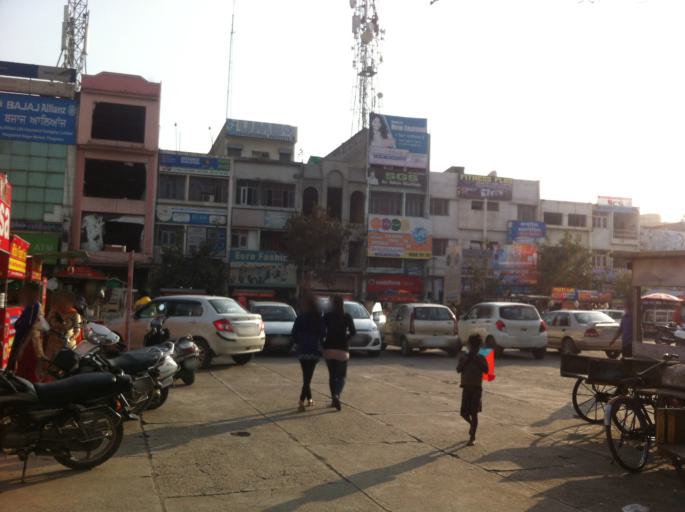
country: IN
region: Punjab
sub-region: Kapurthala
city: Phagwara
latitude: 31.2145
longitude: 75.7737
